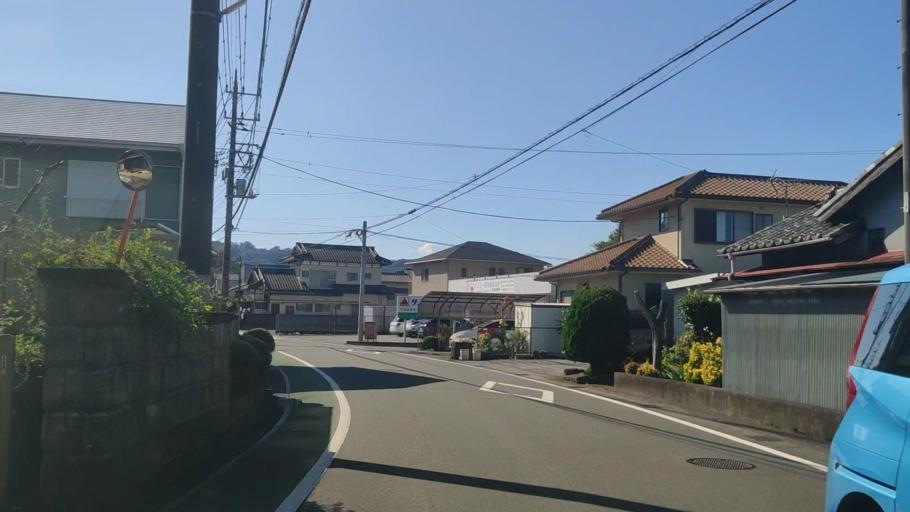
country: JP
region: Shizuoka
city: Mishima
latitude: 35.0032
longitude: 138.9435
